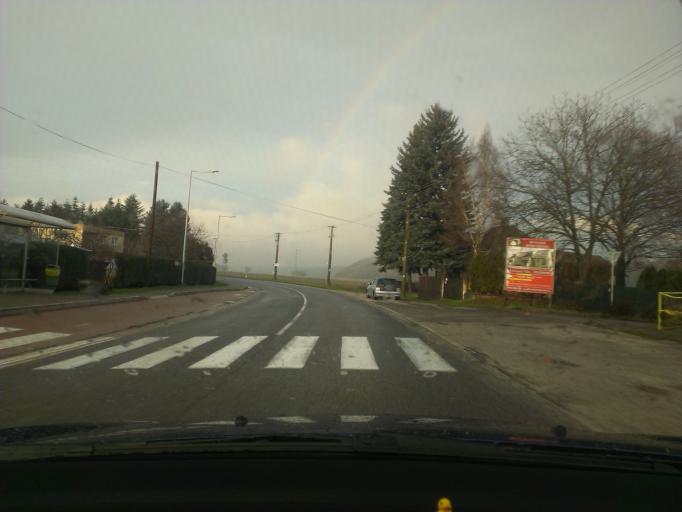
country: SK
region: Trnavsky
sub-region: Okres Trnava
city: Piestany
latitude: 48.6068
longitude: 17.8659
